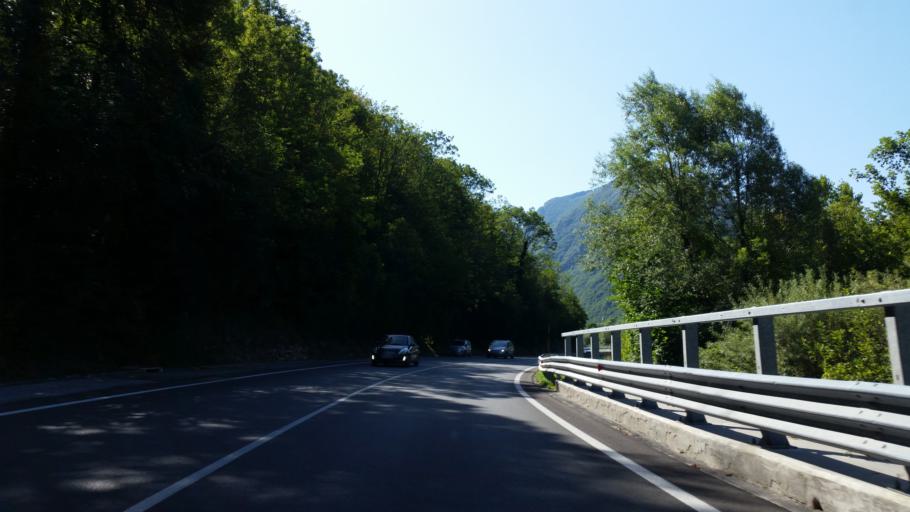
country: IT
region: Piedmont
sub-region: Provincia di Cuneo
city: Vernante
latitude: 44.2529
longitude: 7.5295
